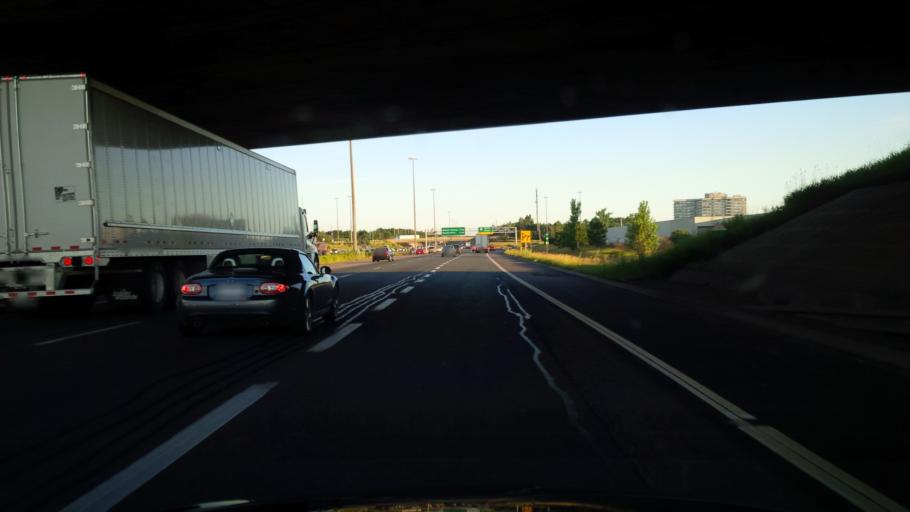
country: CA
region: Ontario
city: Brampton
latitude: 43.7015
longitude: -79.7324
